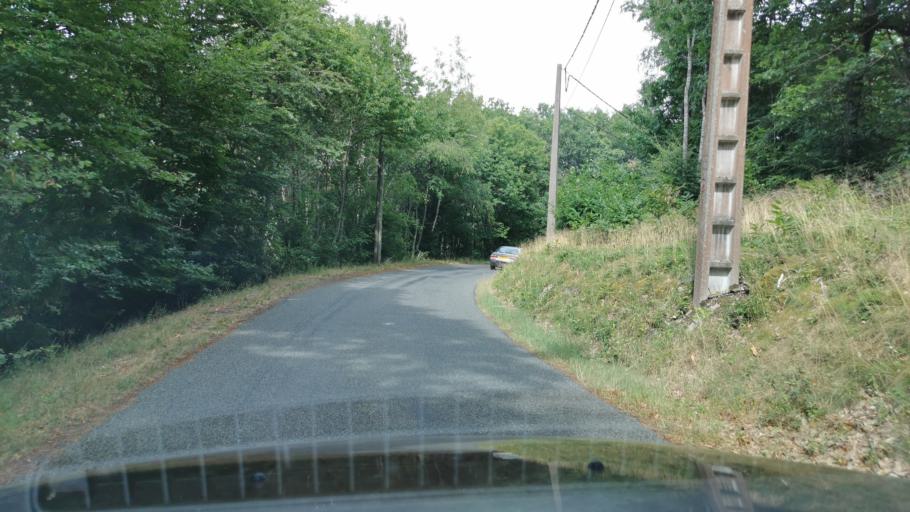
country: FR
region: Bourgogne
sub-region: Departement de Saone-et-Loire
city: Marmagne
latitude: 46.8080
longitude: 4.3019
